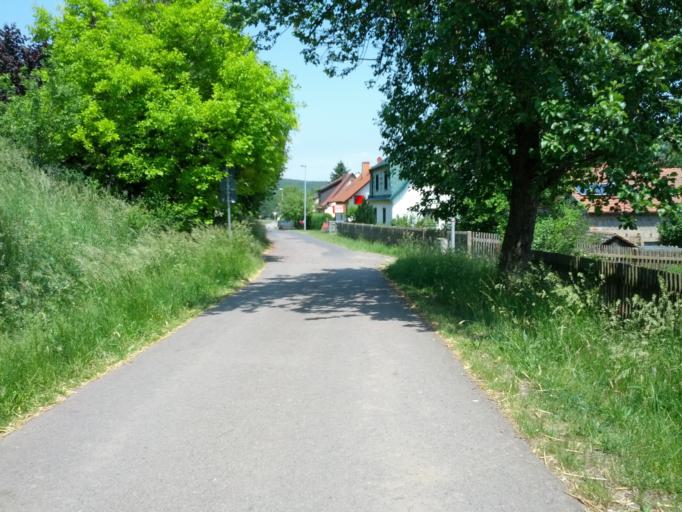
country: DE
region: Thuringia
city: Urnshausen
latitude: 50.7332
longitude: 10.1699
